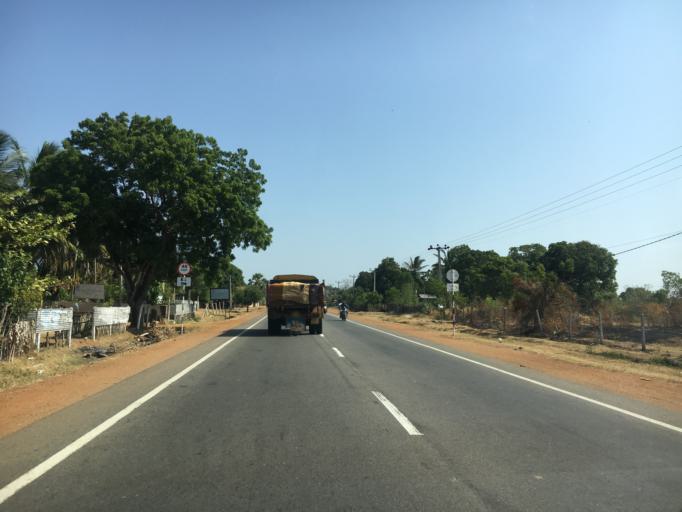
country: LK
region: Northern Province
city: Kilinochchi
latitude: 9.4320
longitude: 80.4077
